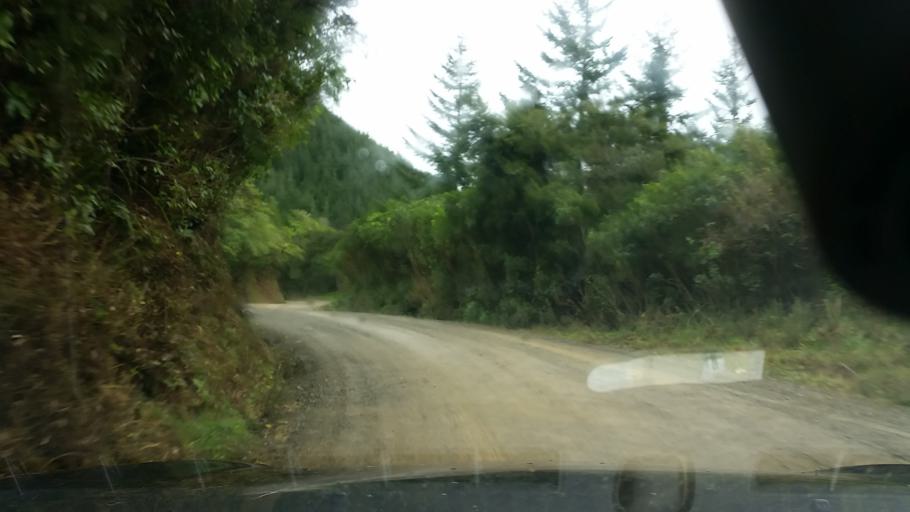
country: NZ
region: Marlborough
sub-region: Marlborough District
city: Picton
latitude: -41.3510
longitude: 174.0786
